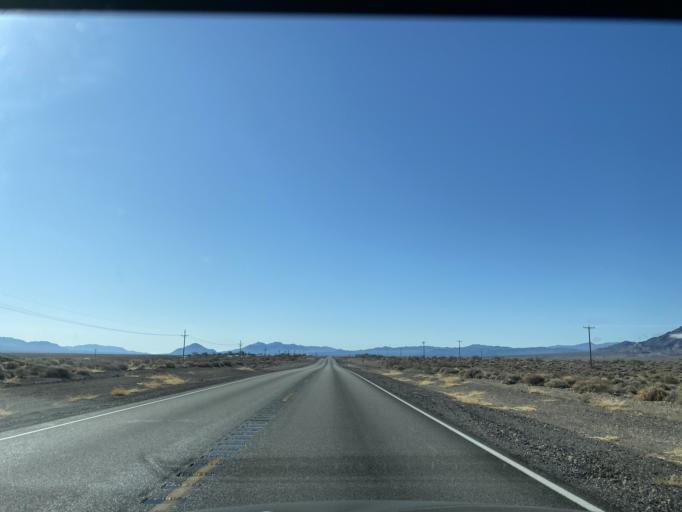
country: US
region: Nevada
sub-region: Nye County
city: Pahrump
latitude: 36.4290
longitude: -116.4222
